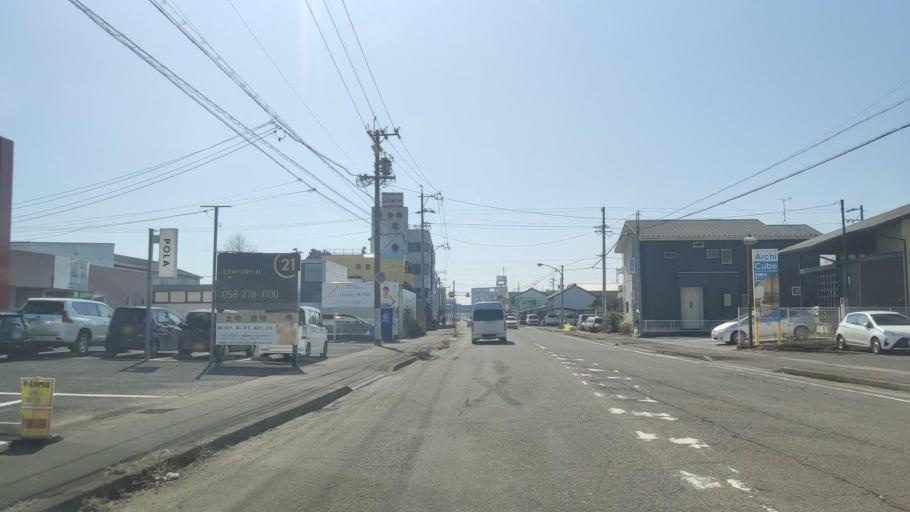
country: JP
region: Gifu
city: Kasamatsucho
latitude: 35.3916
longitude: 136.7644
